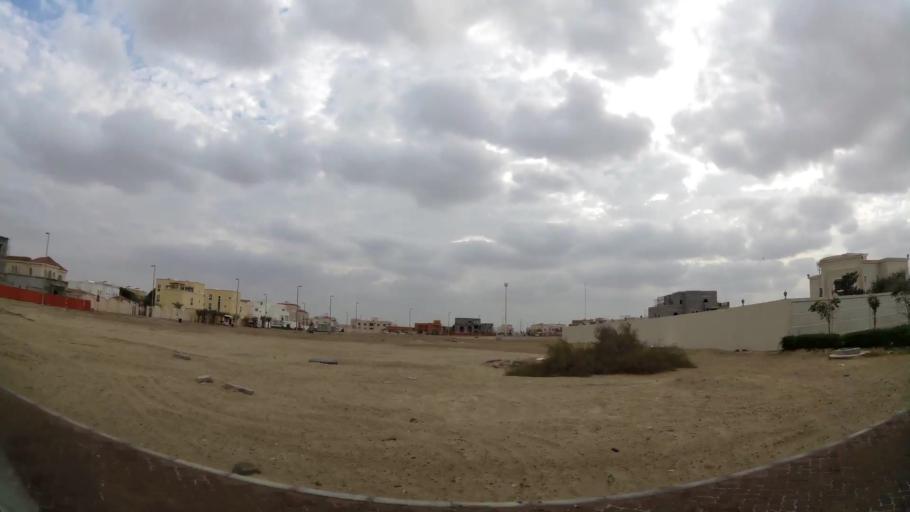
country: AE
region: Abu Dhabi
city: Abu Dhabi
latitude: 24.3485
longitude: 54.6182
